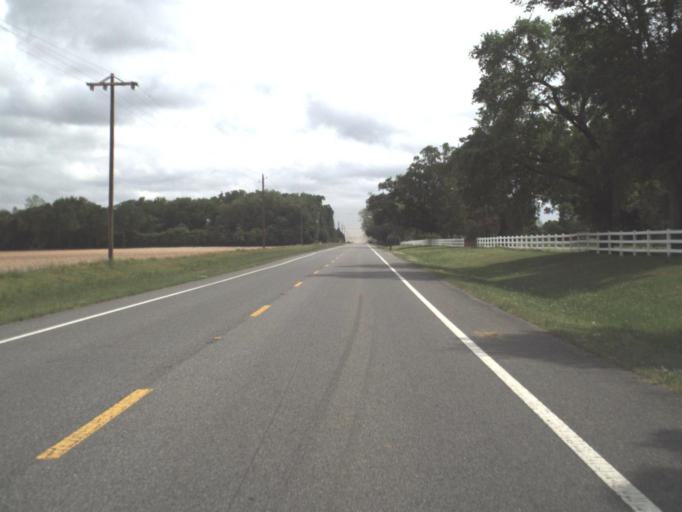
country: US
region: Florida
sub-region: Santa Rosa County
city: Point Baker
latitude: 30.7629
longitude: -87.0931
